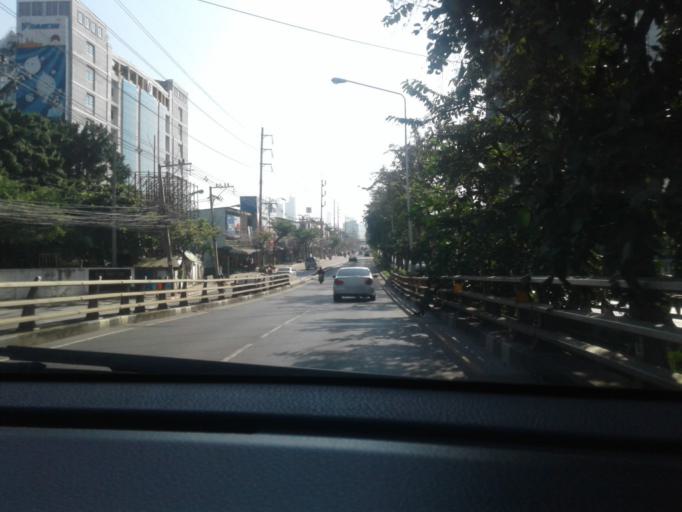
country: TH
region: Bangkok
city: Bangkok Yai
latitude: 13.7291
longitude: 100.4765
